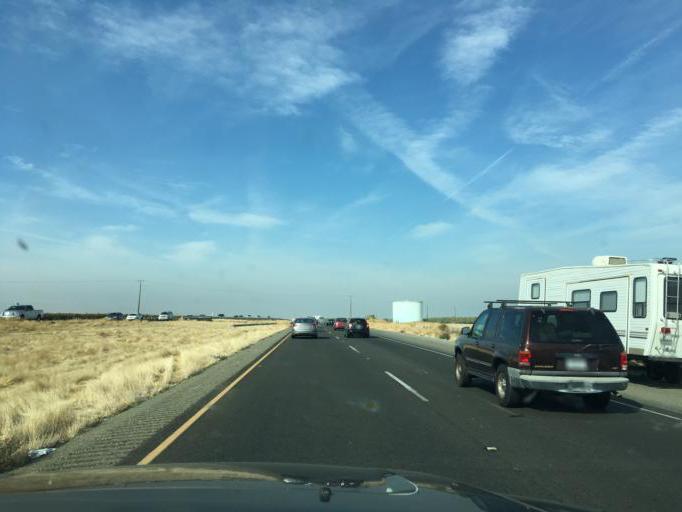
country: US
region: California
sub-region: Fresno County
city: Coalinga
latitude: 36.3512
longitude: -120.3184
